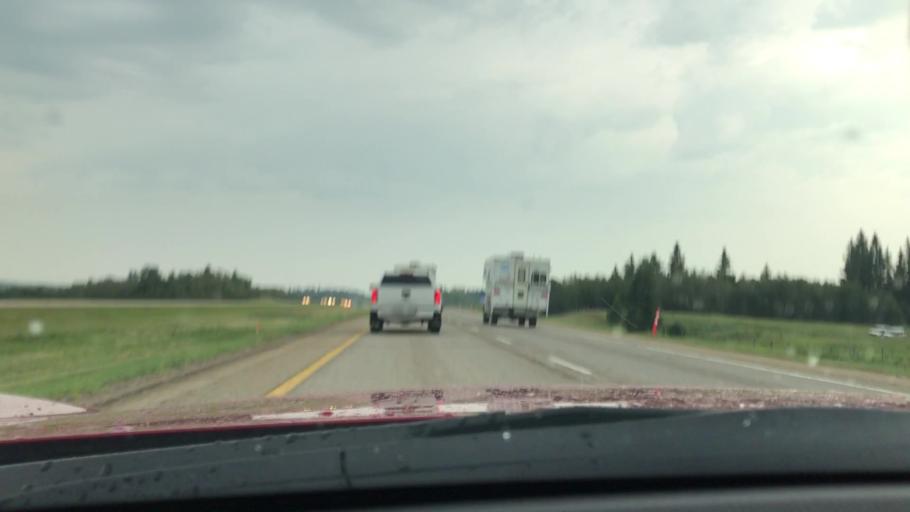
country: CA
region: Alberta
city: Ponoka
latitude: 52.6077
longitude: -113.6636
